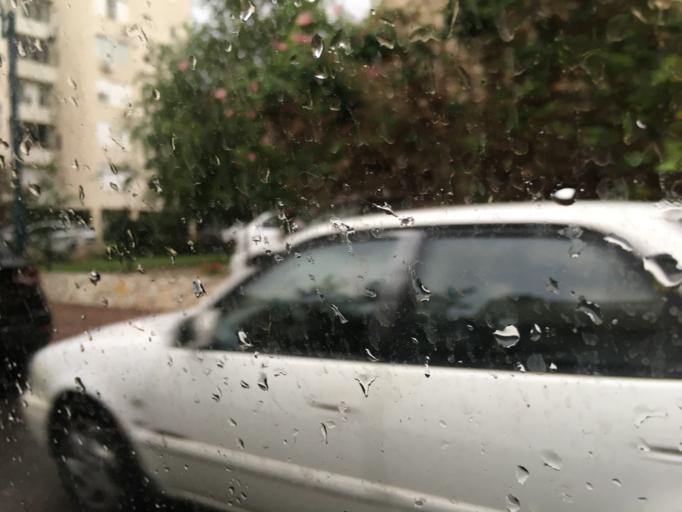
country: IL
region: Tel Aviv
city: Ramat HaSharon
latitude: 32.1410
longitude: 34.8382
